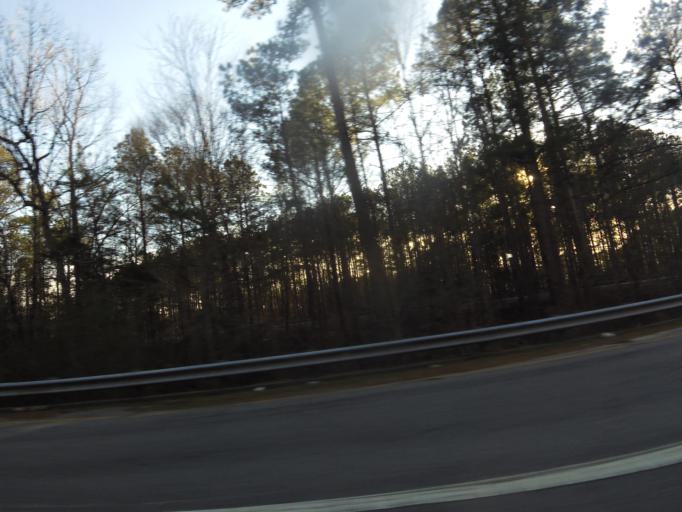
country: US
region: Virginia
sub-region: City of Franklin
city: Franklin
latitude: 36.6490
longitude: -76.8739
